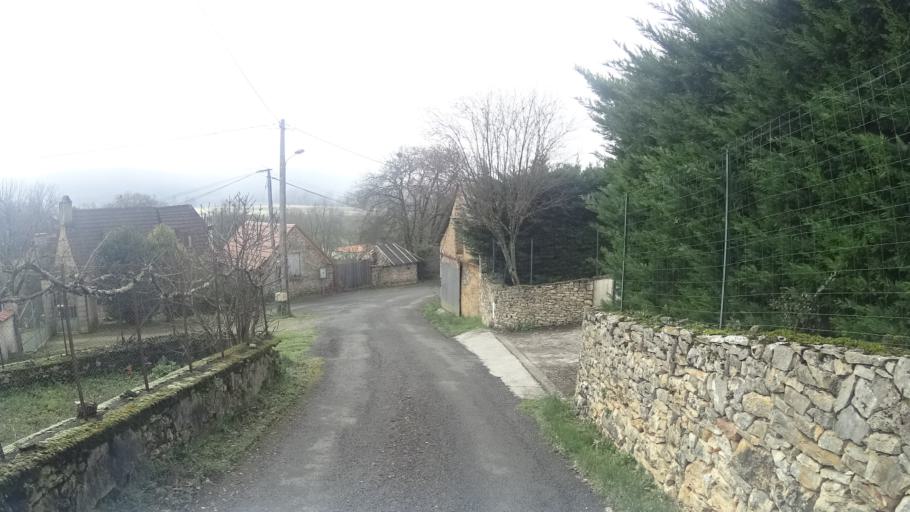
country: FR
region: Aquitaine
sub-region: Departement de la Dordogne
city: Montignac
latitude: 45.1035
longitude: 1.2277
